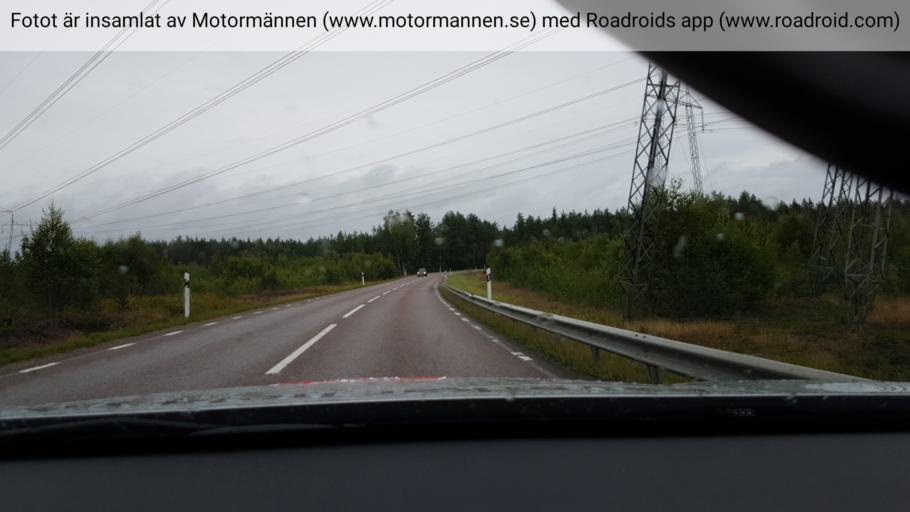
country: SE
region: Gaevleborg
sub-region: Gavle Kommun
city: Valbo
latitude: 60.6036
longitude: 16.9740
